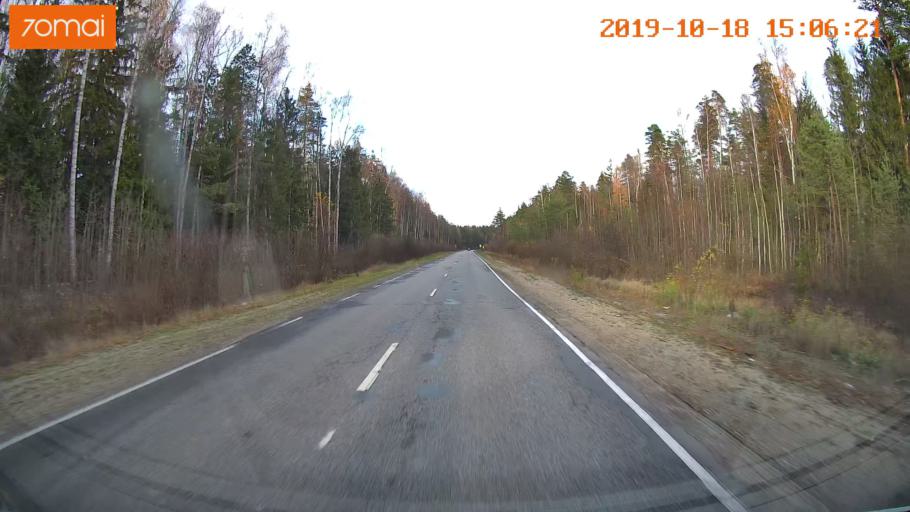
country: RU
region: Vladimir
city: Gus'-Khrustal'nyy
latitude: 55.5287
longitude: 40.5779
